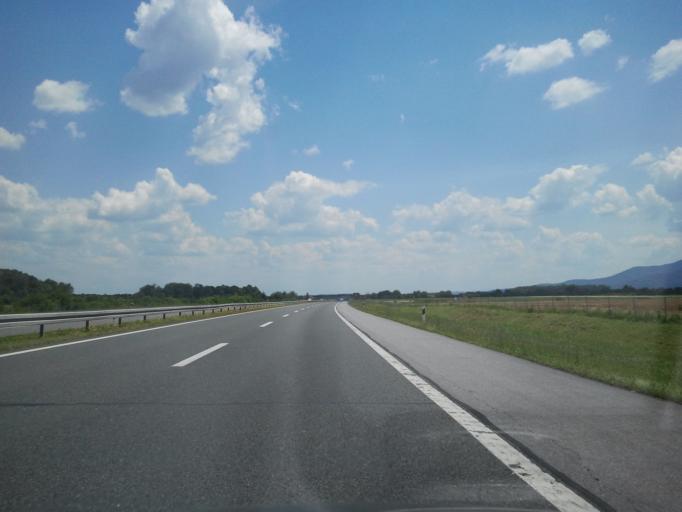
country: HR
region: Brodsko-Posavska
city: Batrina
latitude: 45.1847
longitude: 17.6400
